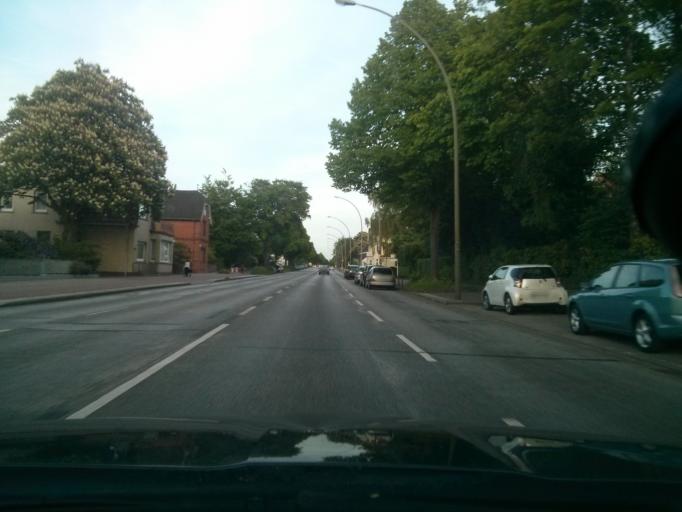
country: DE
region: Schleswig-Holstein
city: Rellingen
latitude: 53.5801
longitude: 9.7981
